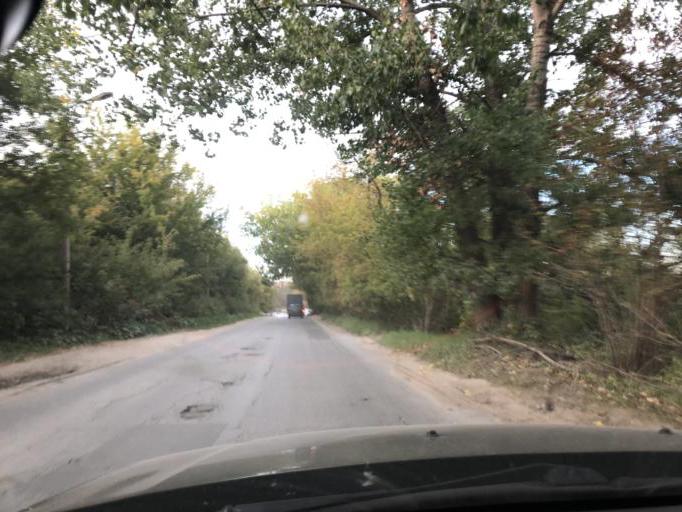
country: RU
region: Tula
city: Tula
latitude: 54.1612
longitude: 37.6172
